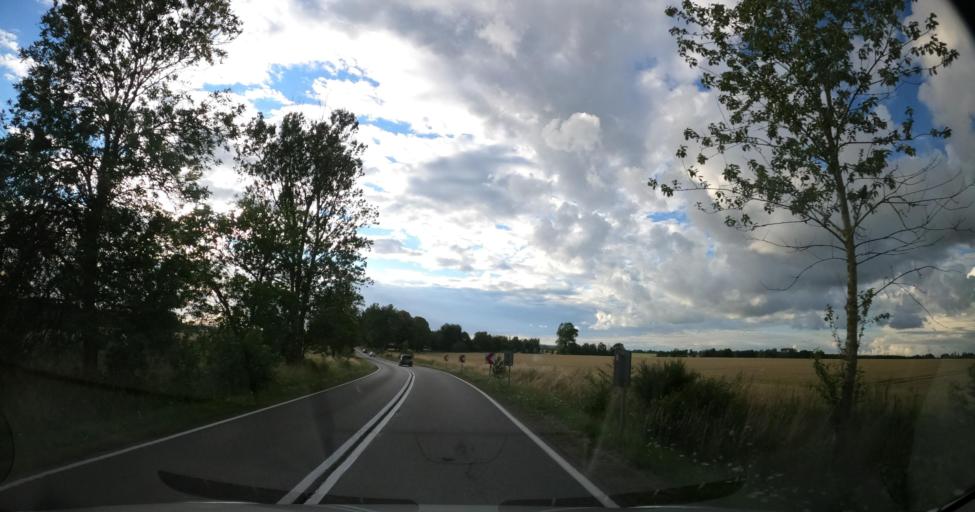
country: PL
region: Pomeranian Voivodeship
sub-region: Powiat slupski
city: Damnica
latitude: 54.4316
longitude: 17.3610
